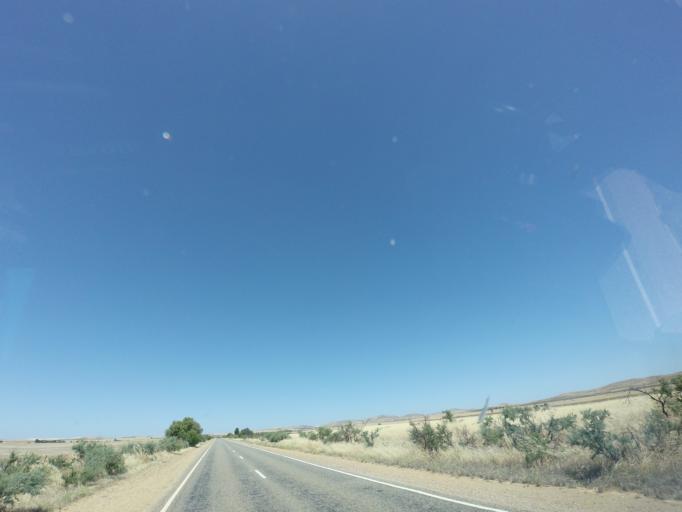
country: AU
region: South Australia
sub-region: Peterborough
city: Peterborough
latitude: -32.7144
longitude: 138.4651
